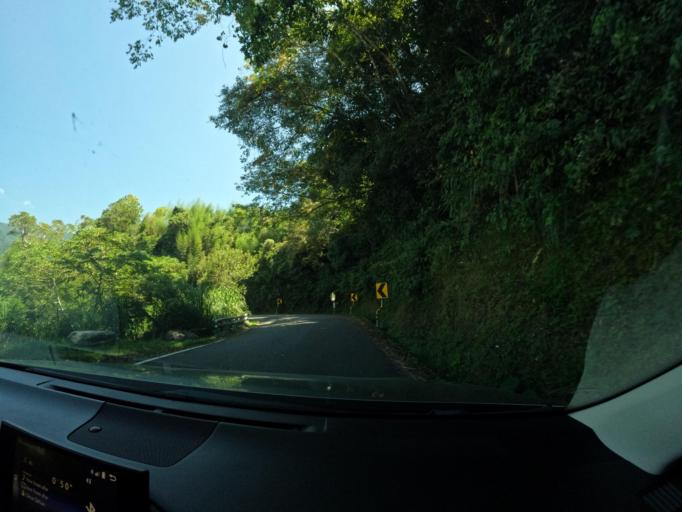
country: TW
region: Taiwan
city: Yujing
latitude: 23.2849
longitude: 120.8411
